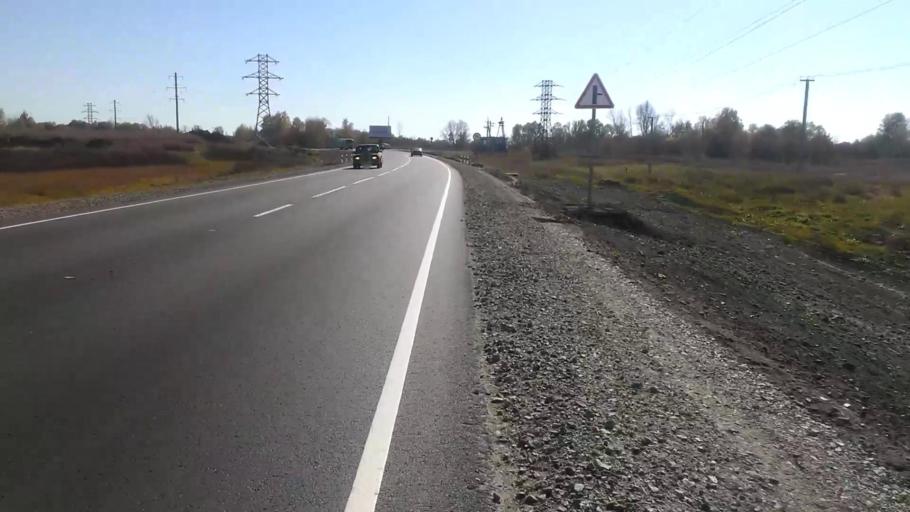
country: RU
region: Altai Krai
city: Sannikovo
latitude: 53.3309
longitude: 83.9384
